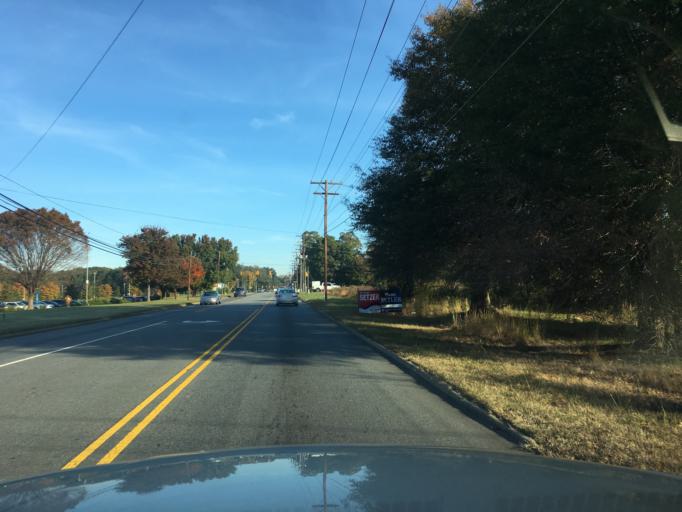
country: US
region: North Carolina
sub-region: Catawba County
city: Conover
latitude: 35.7129
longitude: -81.2649
